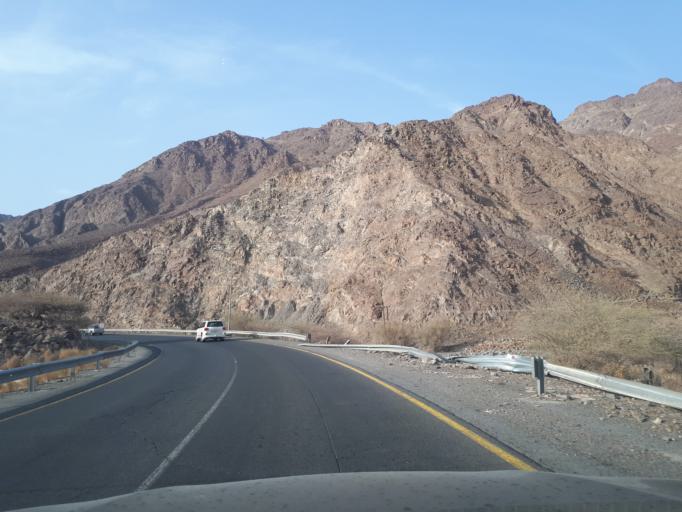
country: OM
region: Muhafazat ad Dakhiliyah
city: Sufalat Sama'il
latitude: 23.1787
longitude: 58.0990
